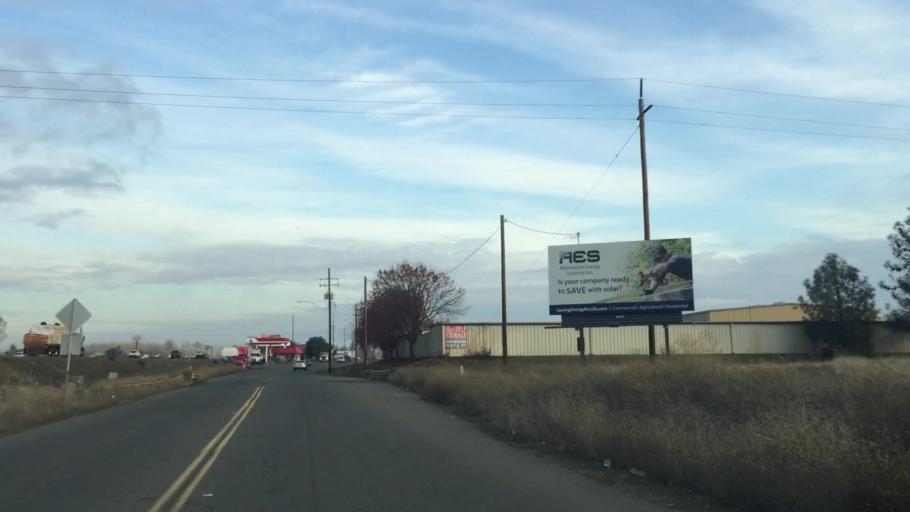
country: US
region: California
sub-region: Butte County
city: South Oroville
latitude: 39.4783
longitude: -121.5752
